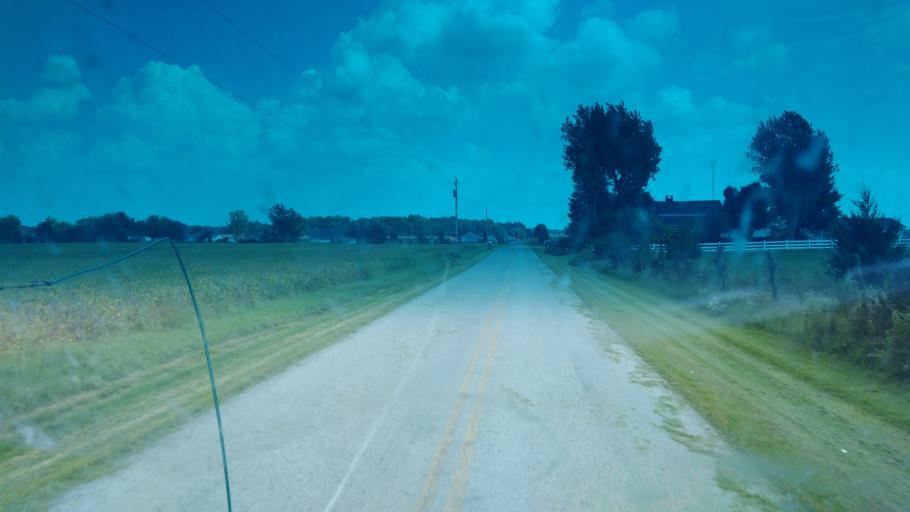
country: US
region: Ohio
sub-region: Hardin County
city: Ada
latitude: 40.7185
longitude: -83.7902
